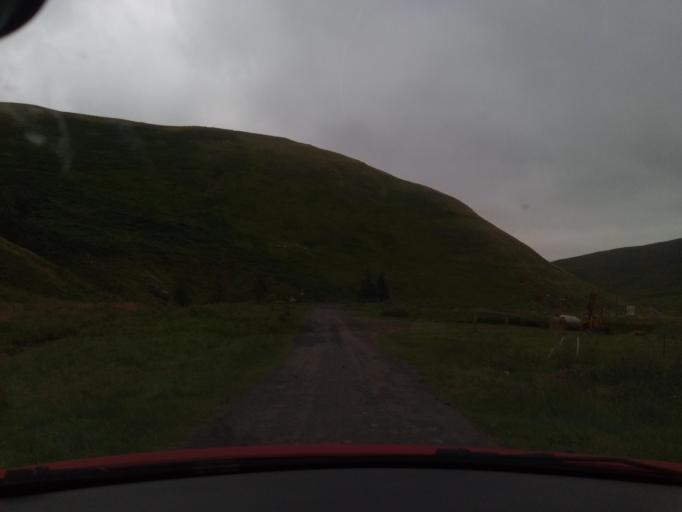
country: GB
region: England
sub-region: Northumberland
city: Rochester
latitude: 55.3973
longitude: -2.2462
